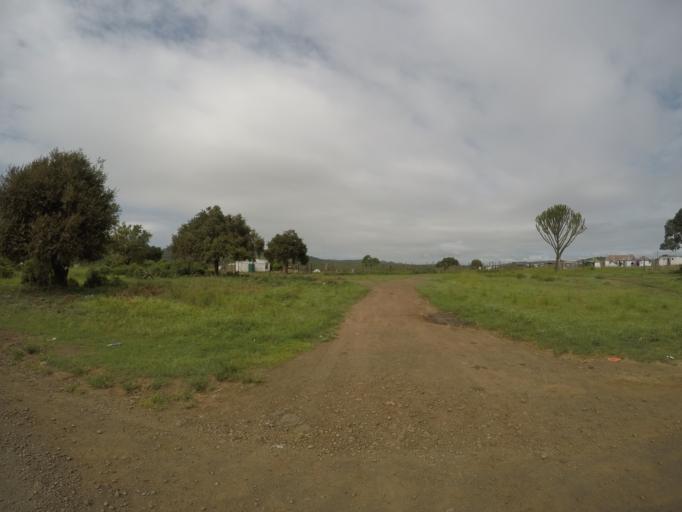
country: ZA
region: KwaZulu-Natal
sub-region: uThungulu District Municipality
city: Empangeni
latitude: -28.6155
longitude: 31.8488
